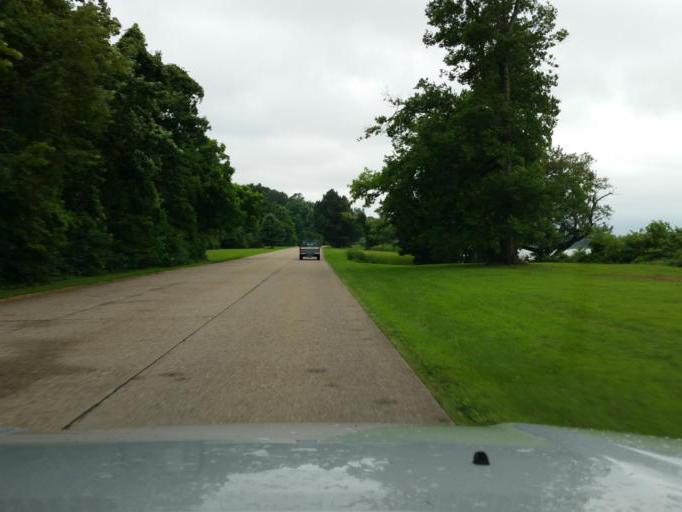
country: US
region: Virginia
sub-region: York County
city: Yorktown
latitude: 37.2712
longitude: -76.5739
